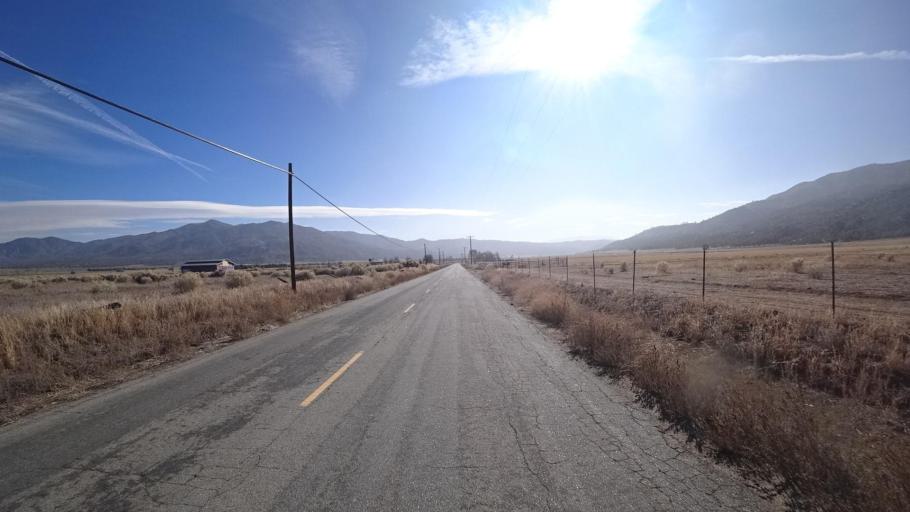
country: US
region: California
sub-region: Kern County
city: Bodfish
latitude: 35.4212
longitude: -118.5369
